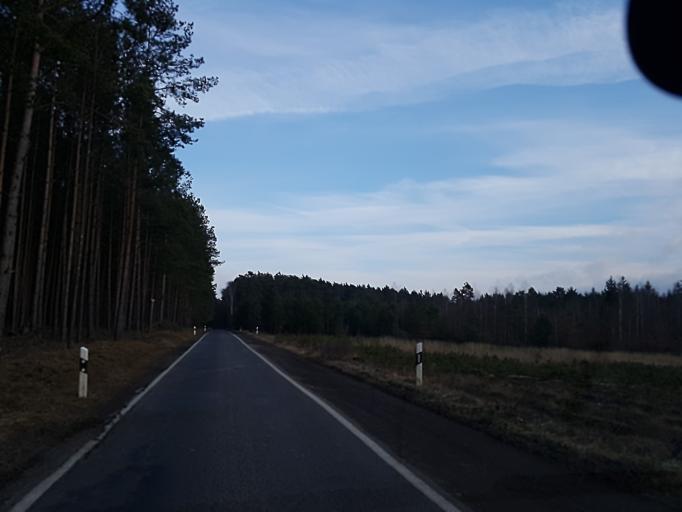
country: DE
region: Brandenburg
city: Wollin
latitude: 52.2395
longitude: 12.5237
